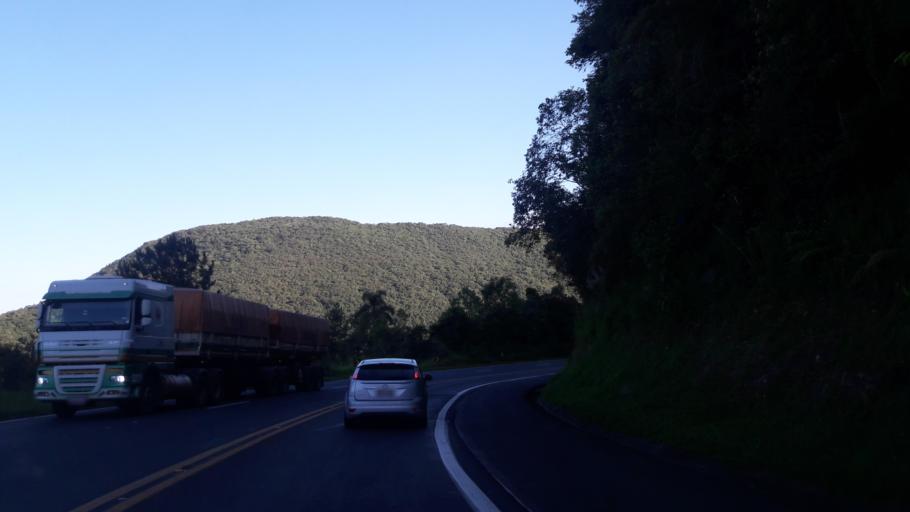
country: BR
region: Parana
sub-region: Prudentopolis
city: Prudentopolis
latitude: -25.3168
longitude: -51.1955
